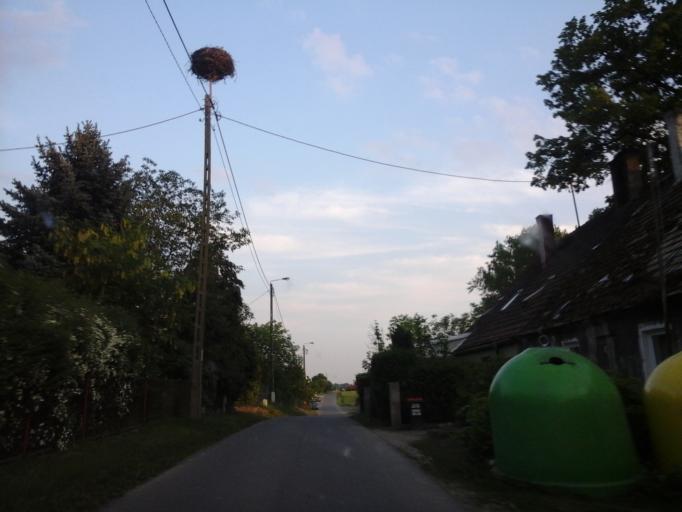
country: PL
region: West Pomeranian Voivodeship
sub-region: Powiat choszczenski
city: Choszczno
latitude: 53.1879
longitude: 15.4160
